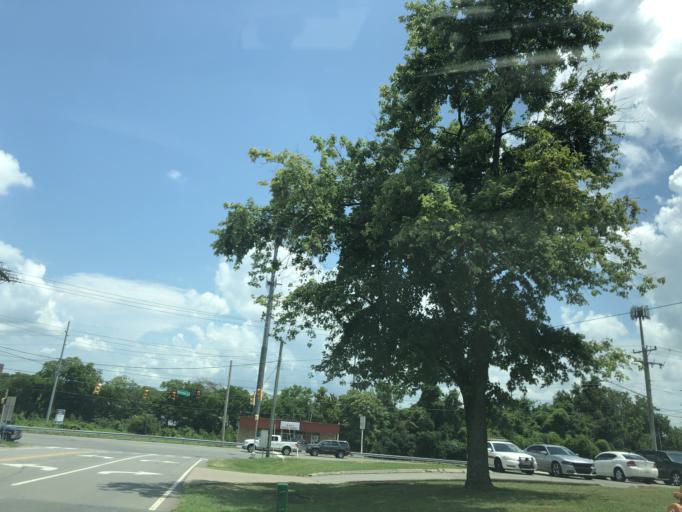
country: US
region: Tennessee
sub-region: Davidson County
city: Lakewood
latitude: 36.2004
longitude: -86.6216
